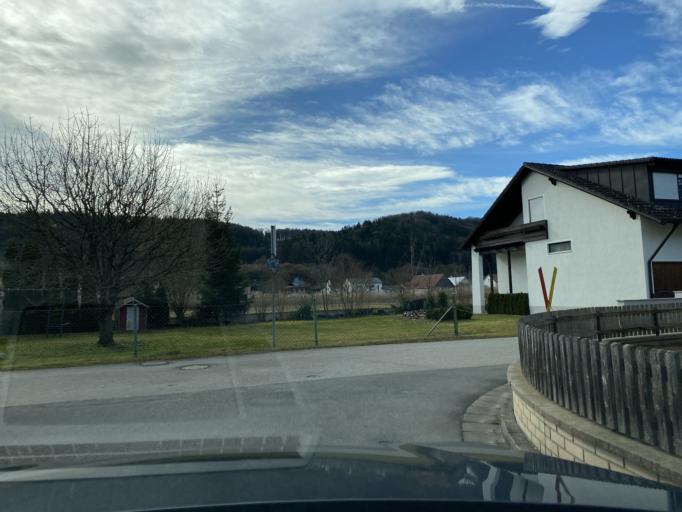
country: DE
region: Bavaria
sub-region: Upper Palatinate
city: Dietfurt
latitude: 49.0183
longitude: 11.5224
